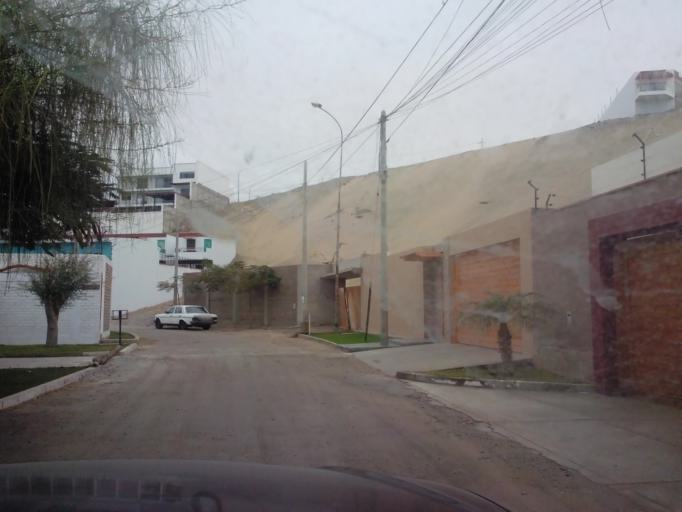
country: PE
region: Ica
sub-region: Provincia de Ica
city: Ica
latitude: -14.0558
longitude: -75.7626
